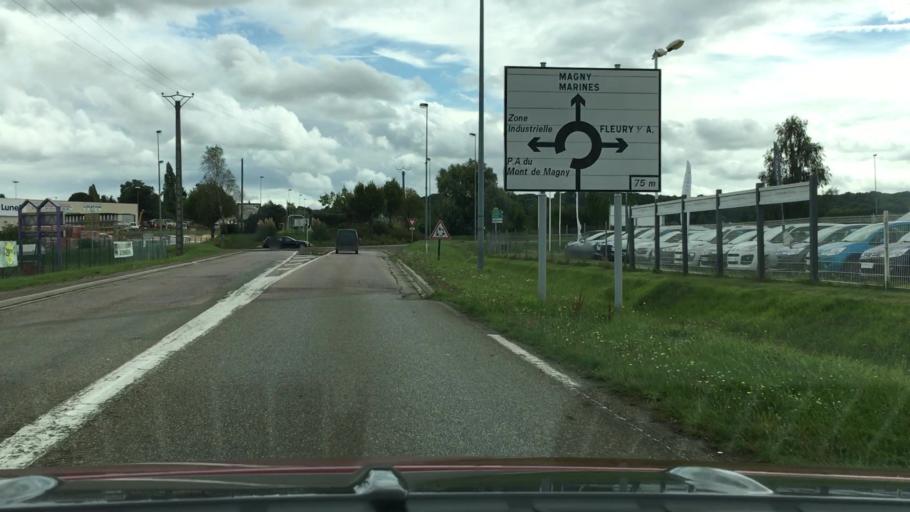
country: FR
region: Haute-Normandie
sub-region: Departement de l'Eure
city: Gisors
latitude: 49.2682
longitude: 1.7830
